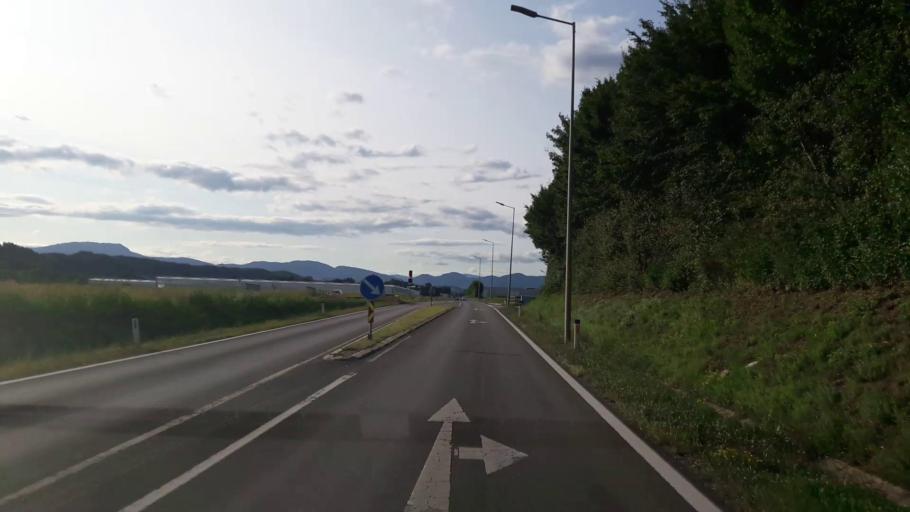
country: AT
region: Styria
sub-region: Politischer Bezirk Weiz
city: Gleisdorf
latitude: 47.1266
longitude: 15.6915
